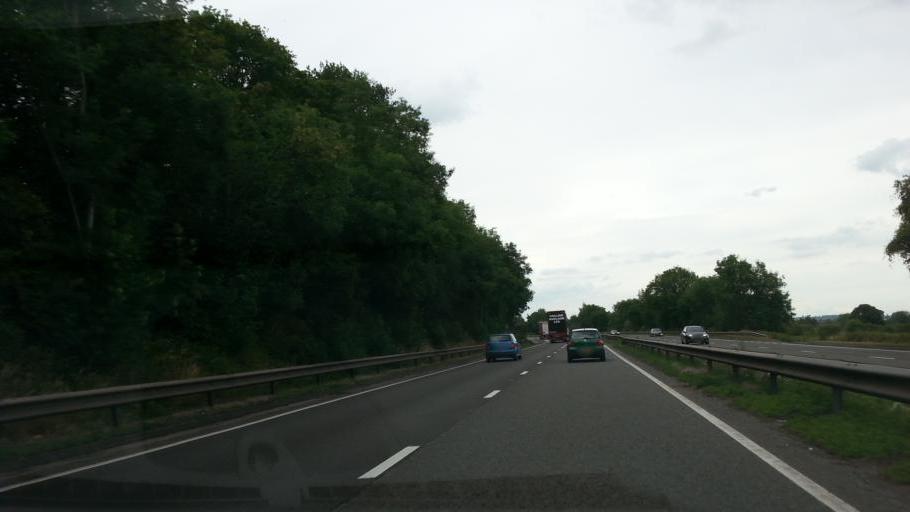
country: GB
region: England
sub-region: Herefordshire
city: Walford
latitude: 51.9016
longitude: -2.6267
